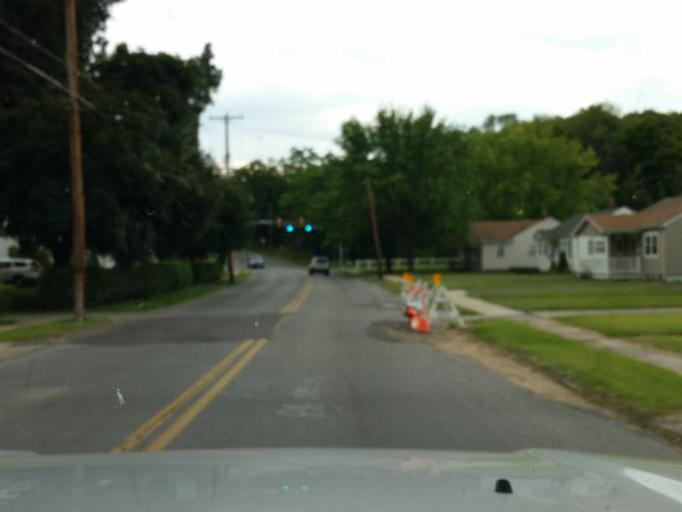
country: US
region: Pennsylvania
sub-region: Blair County
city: Altoona
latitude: 40.5384
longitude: -78.4017
